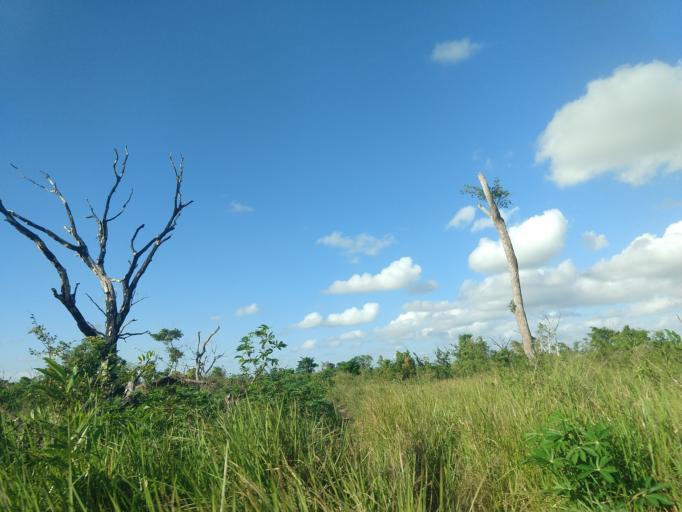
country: MZ
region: Sofala
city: Beira
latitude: -19.5984
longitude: 35.1349
